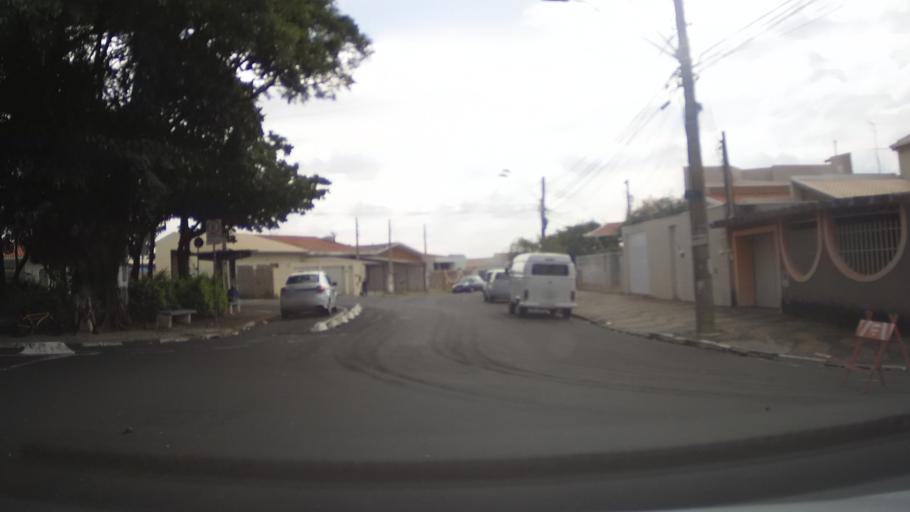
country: BR
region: Sao Paulo
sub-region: Campinas
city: Campinas
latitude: -22.9236
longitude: -47.0577
